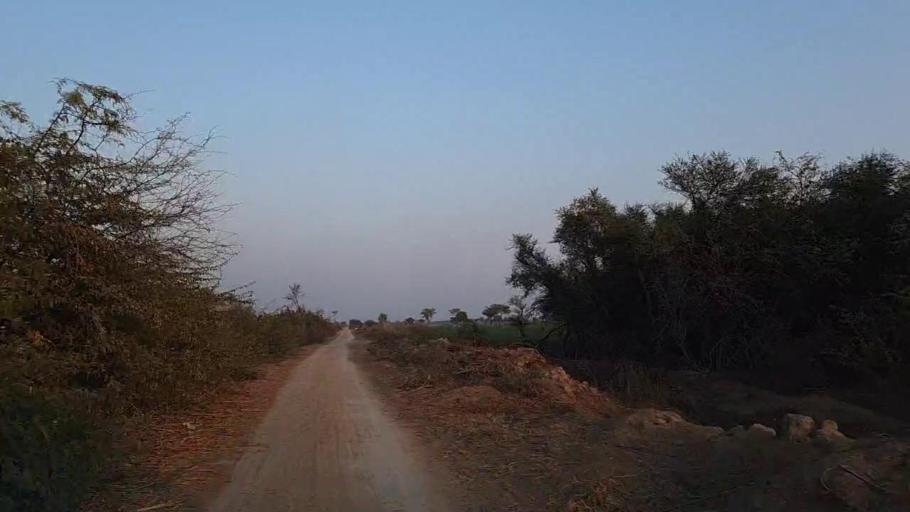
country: PK
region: Sindh
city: Jam Sahib
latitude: 26.3051
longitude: 68.5603
